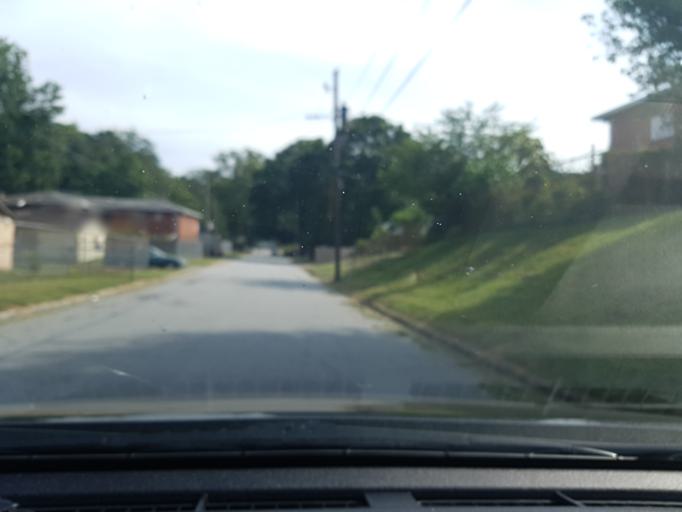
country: US
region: Georgia
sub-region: Fulton County
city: Atlanta
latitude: 33.7710
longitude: -84.4155
